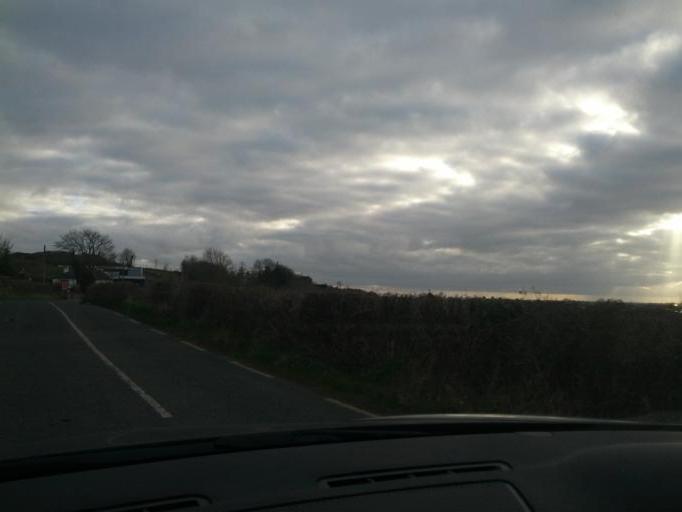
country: IE
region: Leinster
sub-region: Uibh Fhaili
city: Banagher
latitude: 53.3134
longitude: -8.0005
